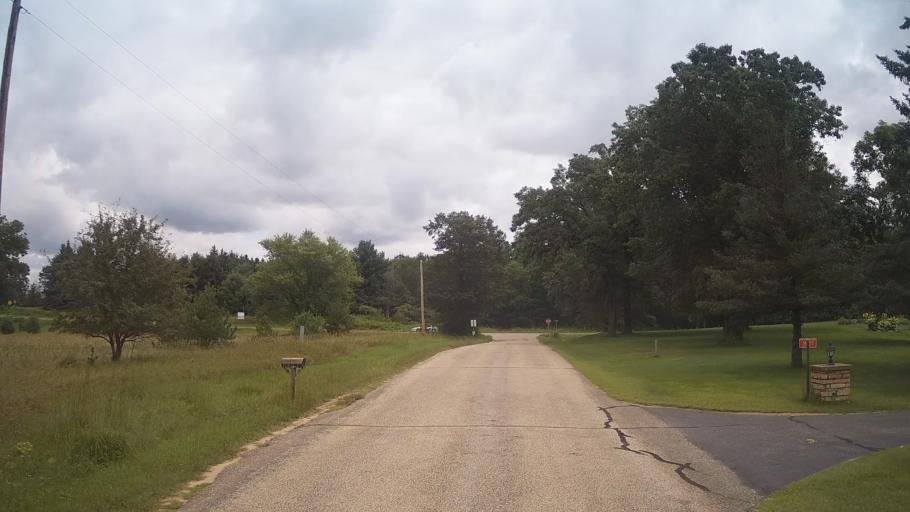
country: US
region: Wisconsin
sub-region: Adams County
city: Friendship
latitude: 44.0326
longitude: -89.8898
